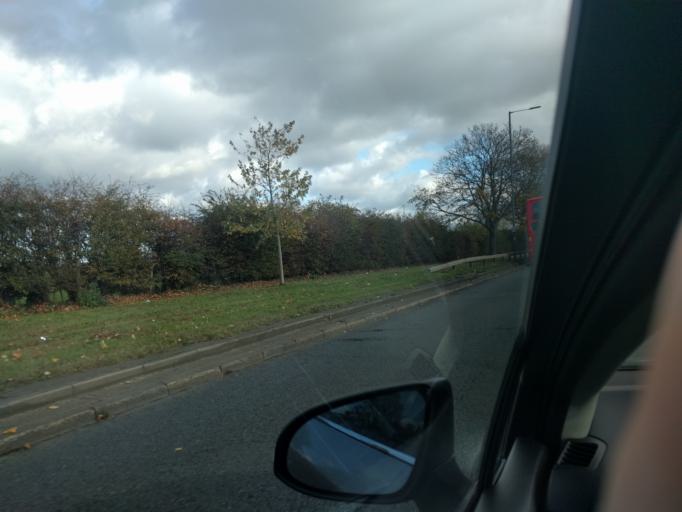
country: GB
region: England
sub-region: Greater London
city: West Drayton
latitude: 51.4818
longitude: -0.4722
